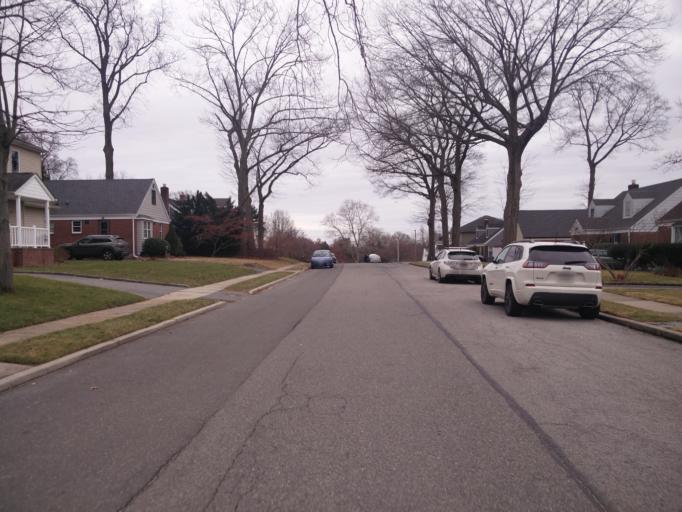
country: US
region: New York
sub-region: Nassau County
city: Glen Cove
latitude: 40.8743
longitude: -73.6259
